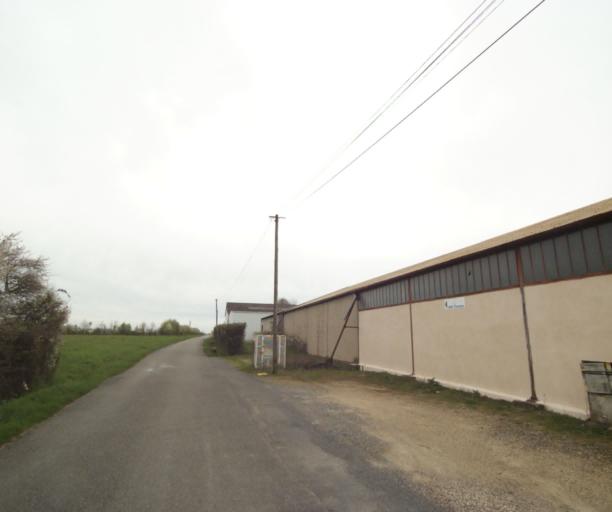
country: FR
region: Bourgogne
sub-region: Departement de Saone-et-Loire
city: Charnay-les-Macon
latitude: 46.2952
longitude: 4.7991
